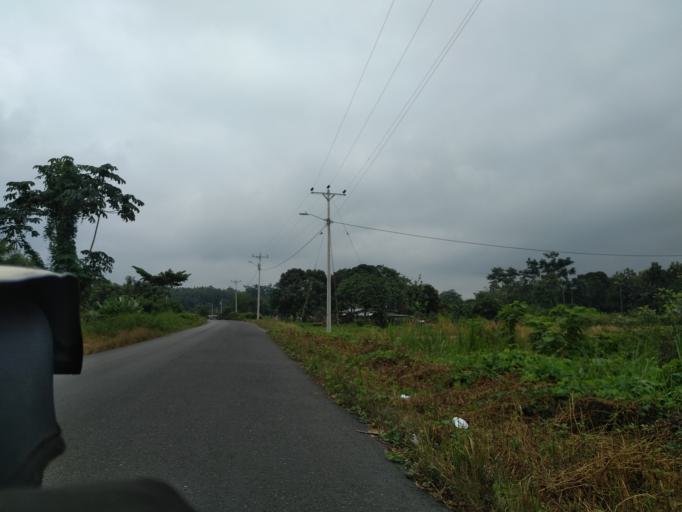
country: EC
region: Los Rios
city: Quevedo
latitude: -0.9774
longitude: -79.3534
